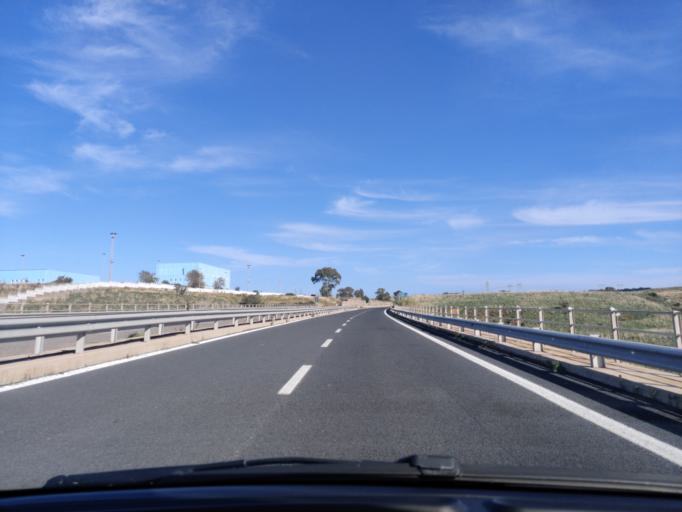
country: IT
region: Latium
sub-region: Citta metropolitana di Roma Capitale
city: Aurelia
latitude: 42.1216
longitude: 11.7908
